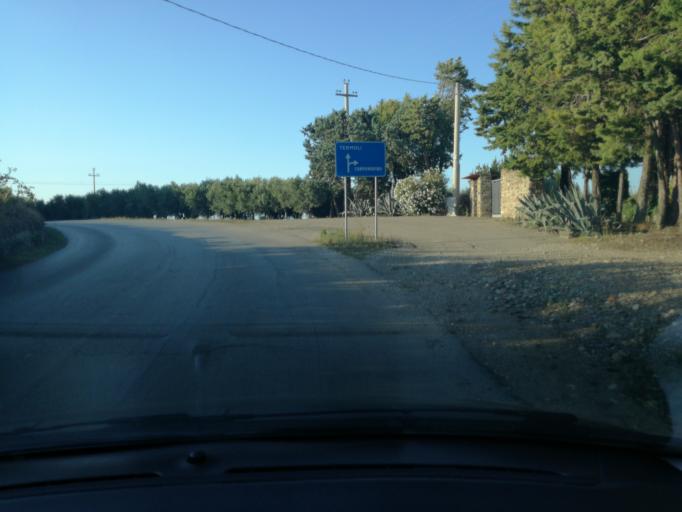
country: IT
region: Molise
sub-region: Provincia di Campobasso
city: San Giacomo degli Schiavoni
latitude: 41.9363
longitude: 14.9461
